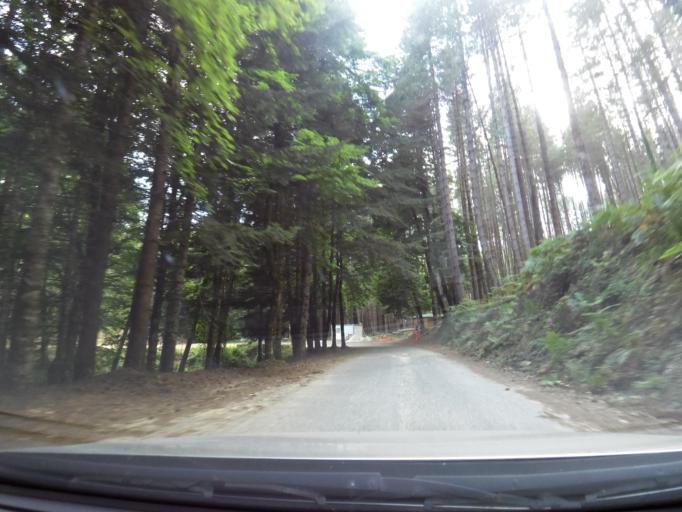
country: IT
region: Calabria
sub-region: Provincia di Vibo-Valentia
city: Nardodipace
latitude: 38.5047
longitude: 16.3762
